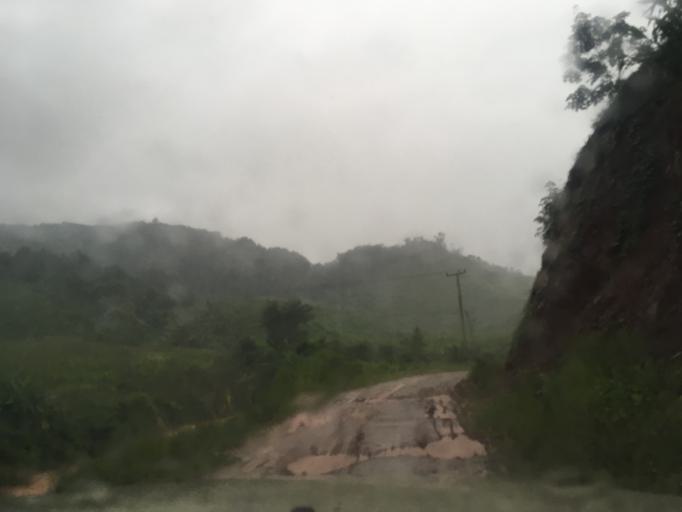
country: LA
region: Oudomxai
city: Muang La
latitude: 21.2332
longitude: 101.9589
